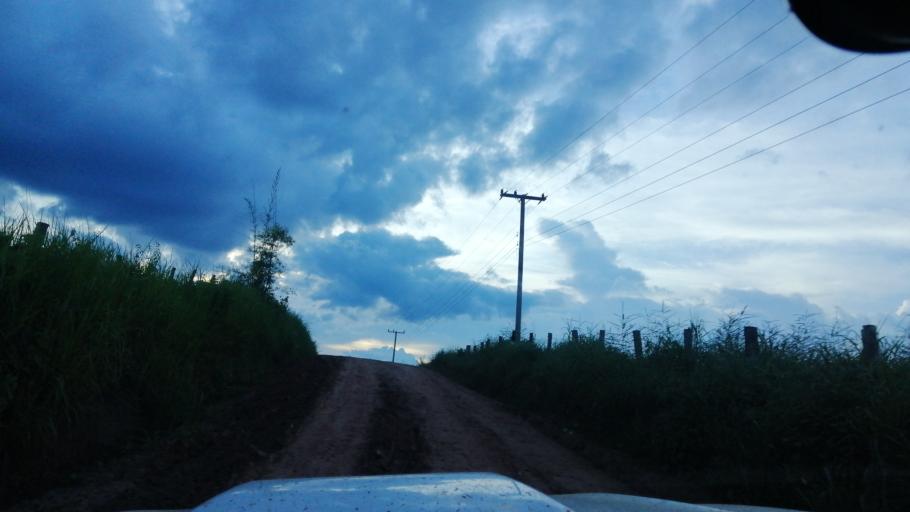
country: TH
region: Uttaradit
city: Ban Khok
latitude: 17.8774
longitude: 101.0697
